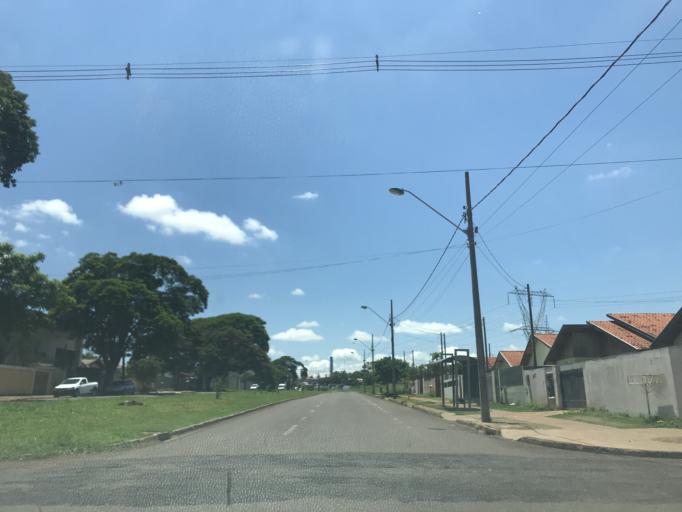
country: BR
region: Parana
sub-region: Maringa
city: Maringa
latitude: -23.4588
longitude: -51.9226
